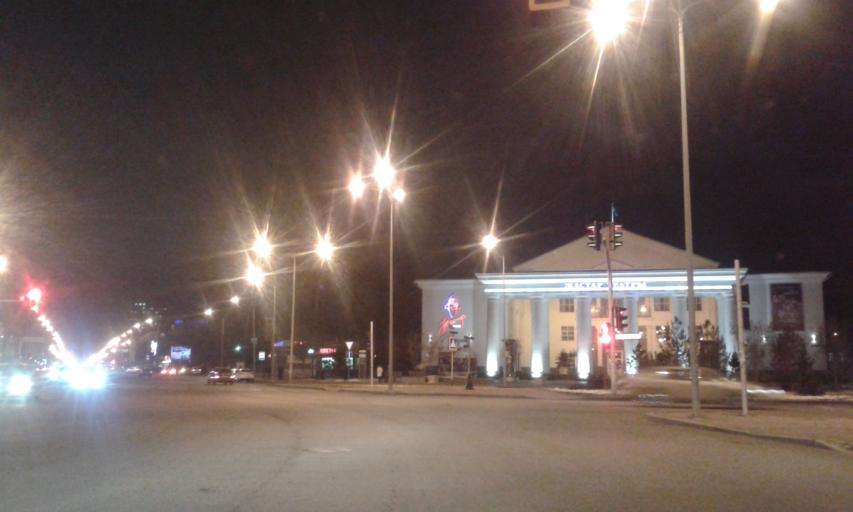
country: KZ
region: Astana Qalasy
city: Astana
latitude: 51.1919
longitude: 71.4066
